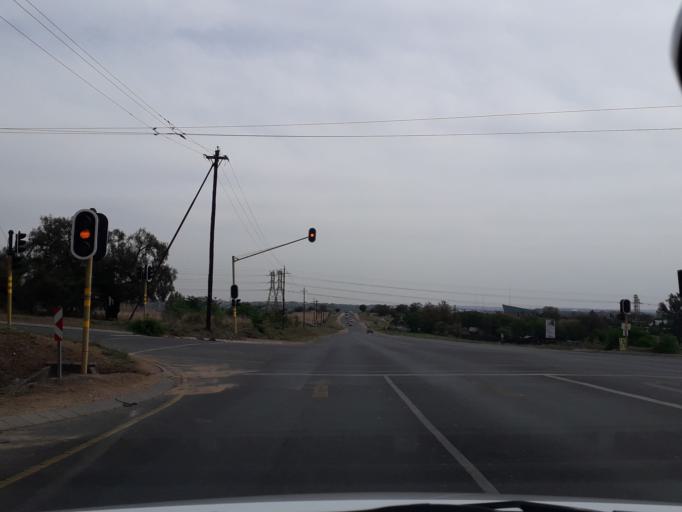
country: ZA
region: Gauteng
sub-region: City of Johannesburg Metropolitan Municipality
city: Diepsloot
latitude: -25.9904
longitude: 28.0513
